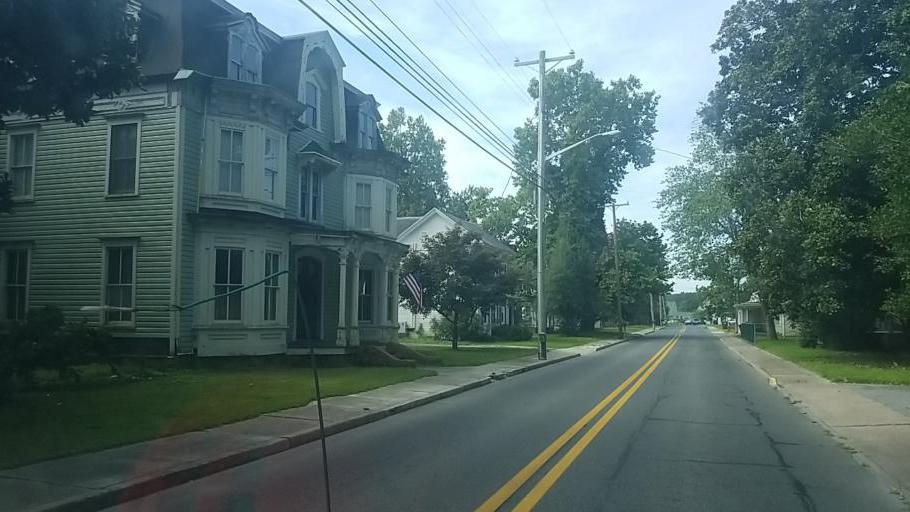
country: US
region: Delaware
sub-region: Sussex County
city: Selbyville
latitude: 38.5178
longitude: -75.2298
